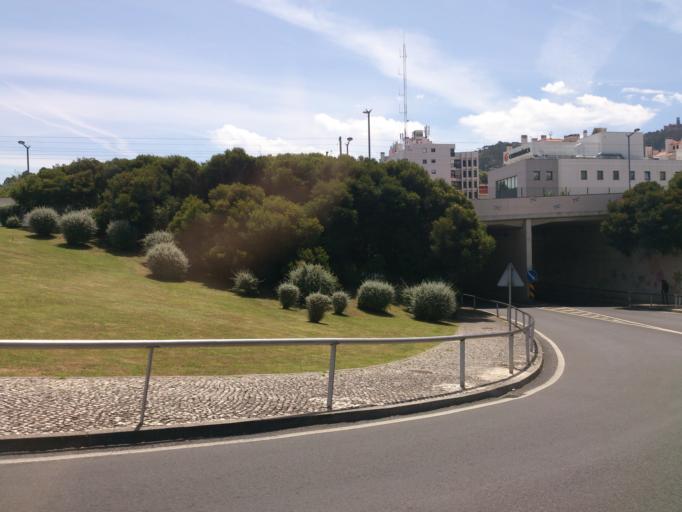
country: PT
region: Lisbon
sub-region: Sintra
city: Sintra
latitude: 38.8029
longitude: -9.3787
